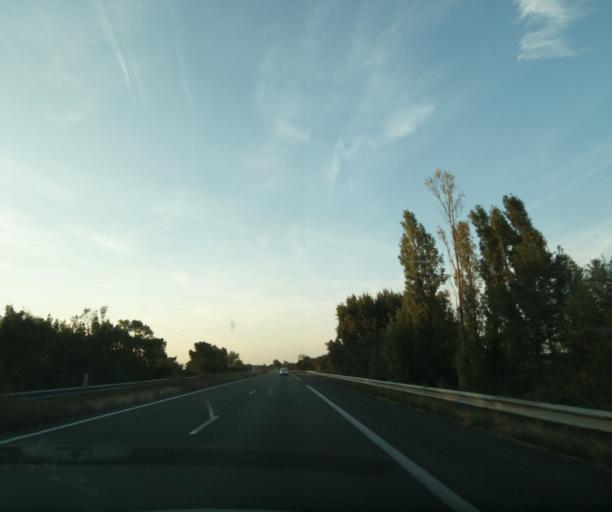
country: FR
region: Aquitaine
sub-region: Departement du Lot-et-Garonne
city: Damazan
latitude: 44.3286
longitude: 0.2578
